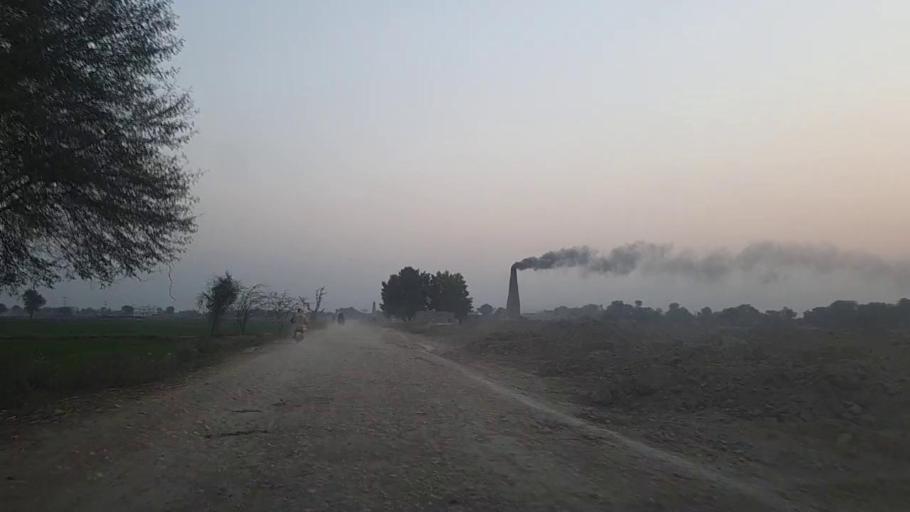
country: PK
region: Sindh
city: Naushahro Firoz
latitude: 26.8556
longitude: 68.0493
